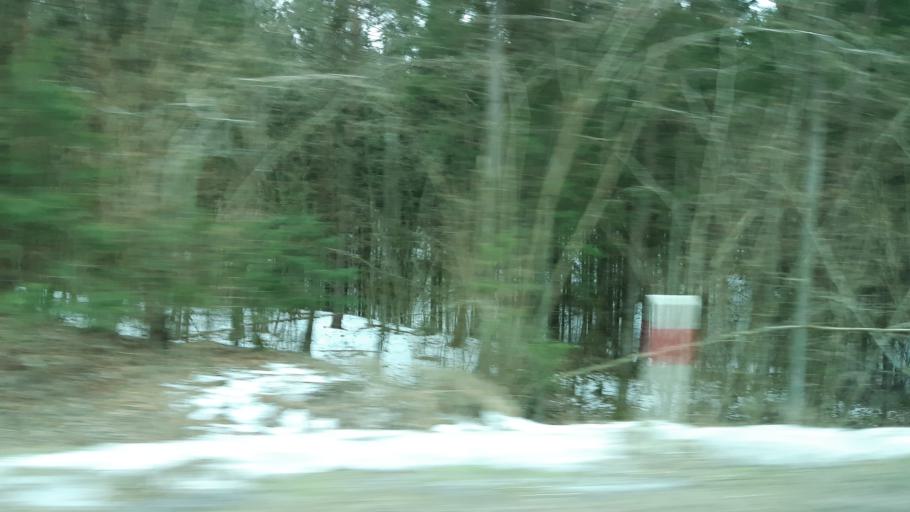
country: PL
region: Podlasie
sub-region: Suwalki
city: Suwalki
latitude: 54.2877
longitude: 22.9540
